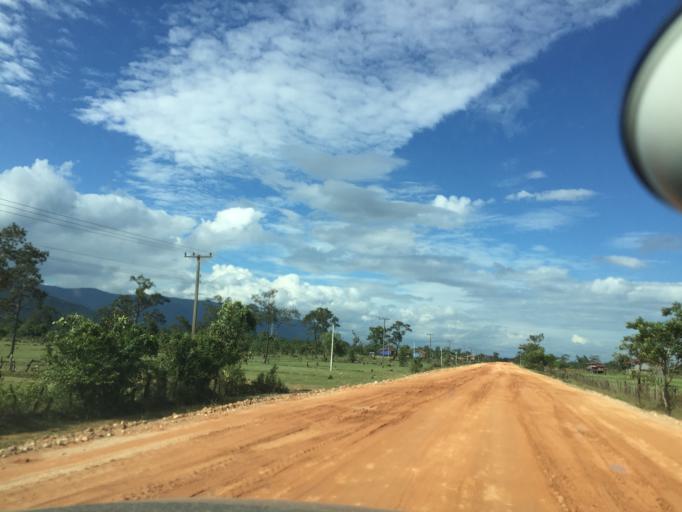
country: LA
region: Attapu
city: Attapu
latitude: 14.6913
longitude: 106.6075
